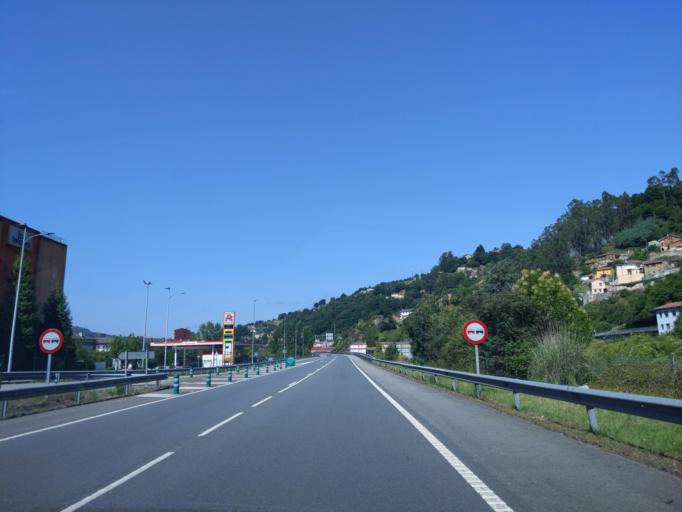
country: ES
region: Asturias
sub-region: Province of Asturias
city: El entrego
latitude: 43.2888
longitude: -5.6319
